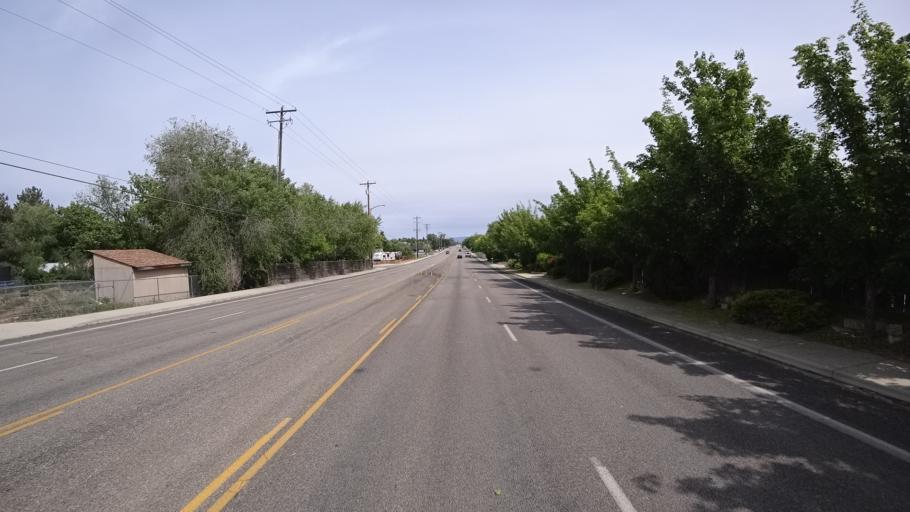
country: US
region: Idaho
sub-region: Ada County
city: Meridian
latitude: 43.5769
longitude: -116.3142
